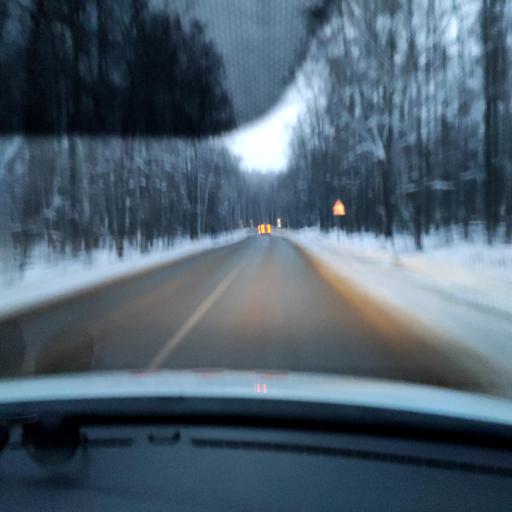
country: RU
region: Tatarstan
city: Vysokaya Gora
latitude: 55.9345
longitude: 49.1714
